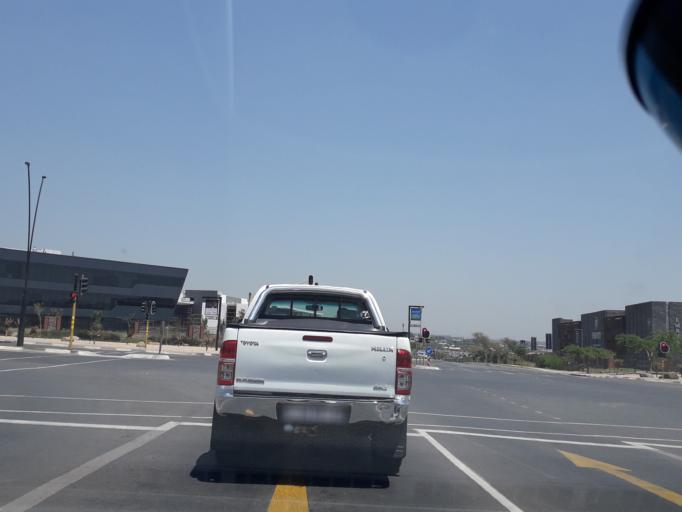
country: ZA
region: Gauteng
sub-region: City of Johannesburg Metropolitan Municipality
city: Midrand
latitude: -26.0135
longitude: 28.0997
